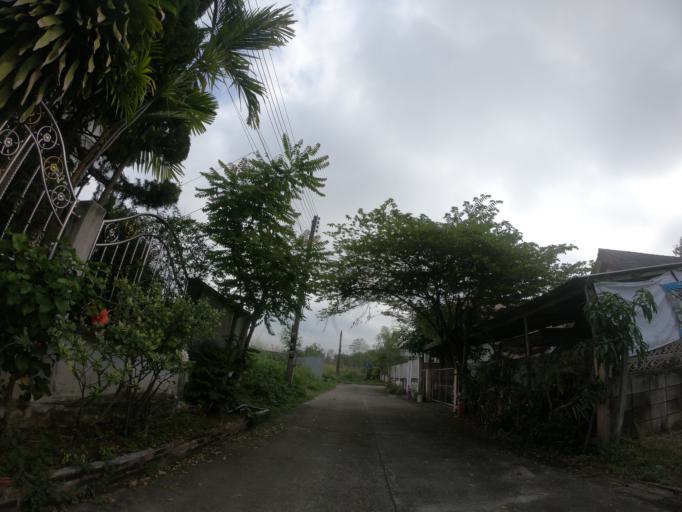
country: TH
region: Chiang Mai
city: Chiang Mai
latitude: 18.7588
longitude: 98.9751
